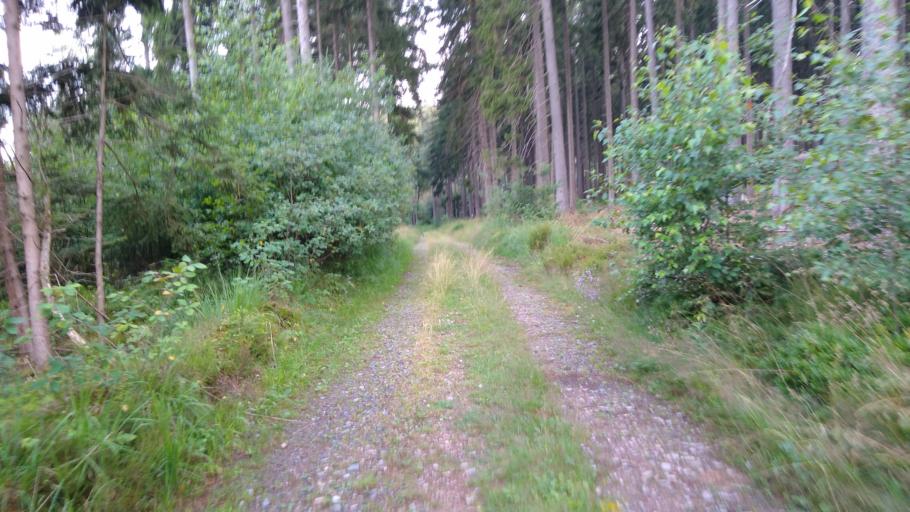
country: DE
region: Hesse
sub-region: Regierungsbezirk Darmstadt
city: Frankisch-Crumbach
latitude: 49.7080
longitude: 8.9145
